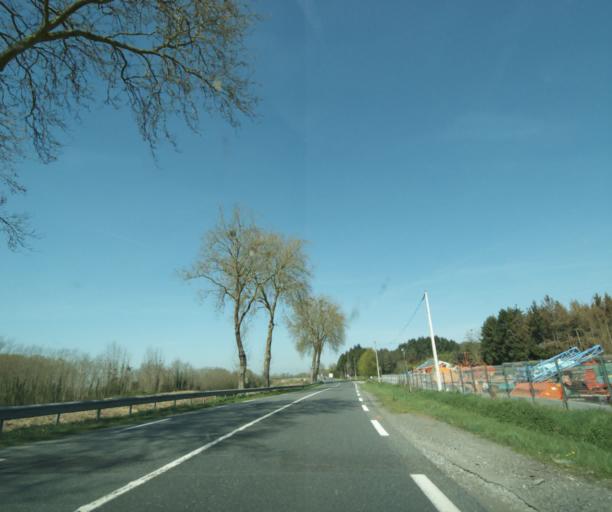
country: FR
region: Bourgogne
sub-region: Departement de la Nievre
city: Chantenay-Saint-Imbert
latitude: 46.6770
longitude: 3.2315
